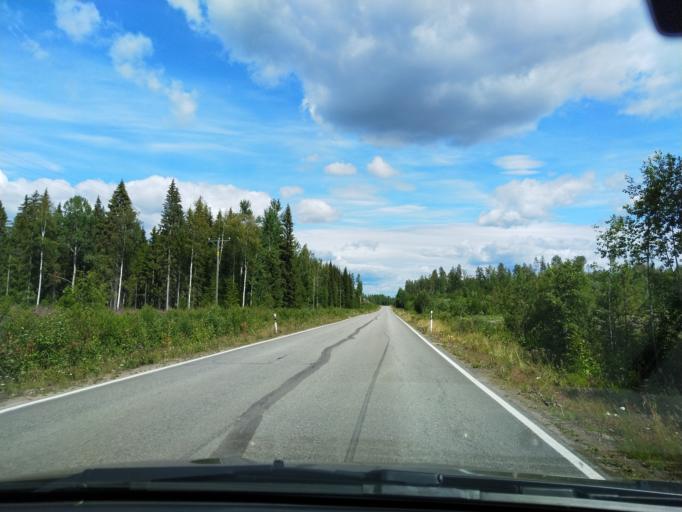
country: FI
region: Kymenlaakso
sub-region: Kouvola
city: Jaala
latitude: 61.0429
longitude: 26.5588
